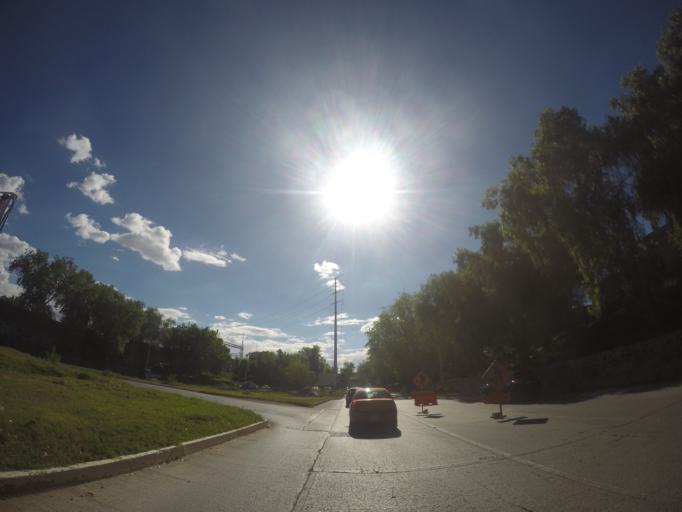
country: MX
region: San Luis Potosi
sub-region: San Luis Potosi
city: San Luis Potosi
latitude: 22.1639
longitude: -100.9891
